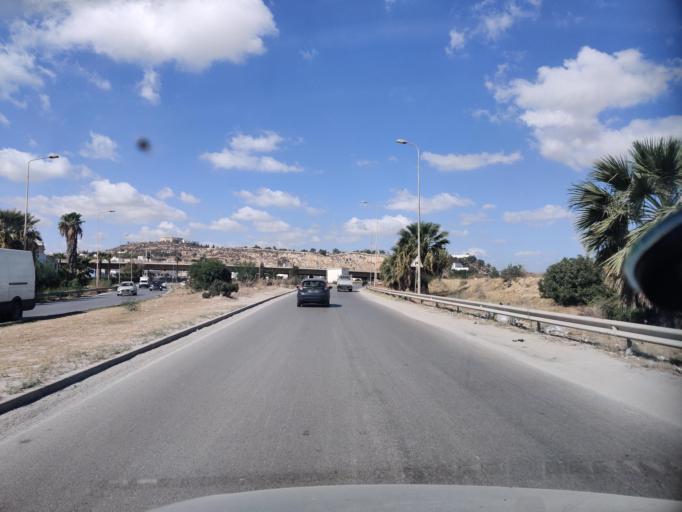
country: TN
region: Bin 'Arus
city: Ben Arous
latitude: 36.7812
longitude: 10.2001
